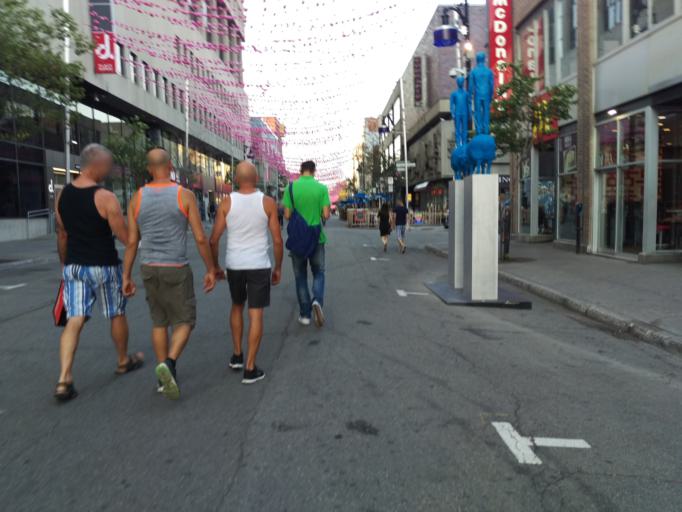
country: CA
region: Quebec
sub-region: Montreal
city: Montreal
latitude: 45.5157
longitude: -73.5587
